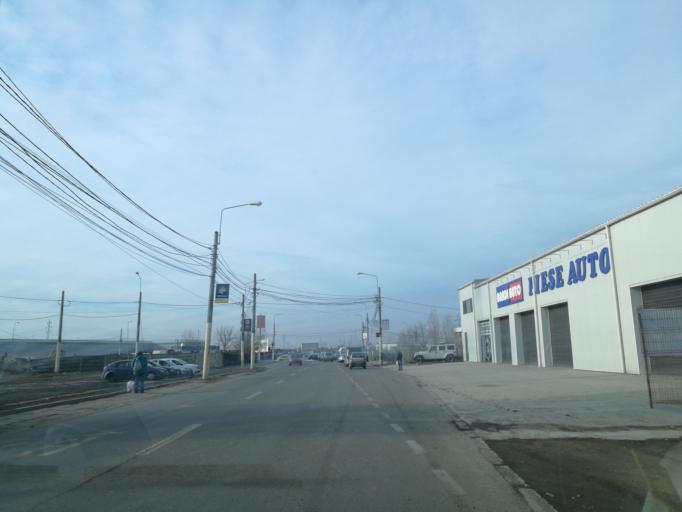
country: RO
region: Constanta
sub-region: Municipiul Constanta
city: Constanta
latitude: 44.1922
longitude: 28.6044
